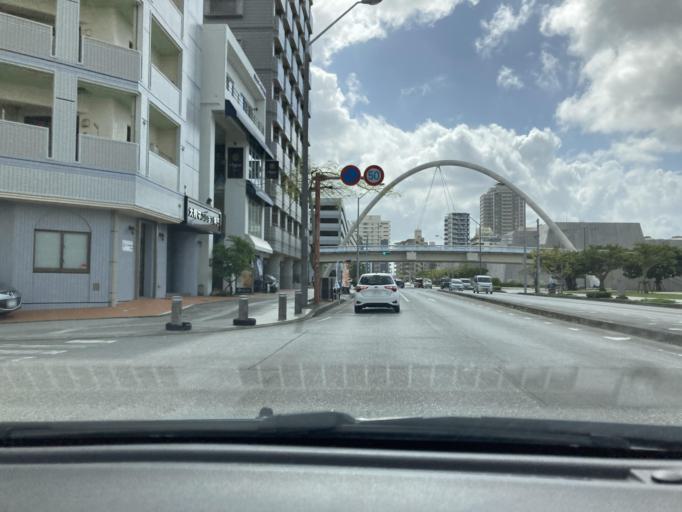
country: JP
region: Okinawa
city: Naha-shi
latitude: 26.2277
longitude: 127.6962
